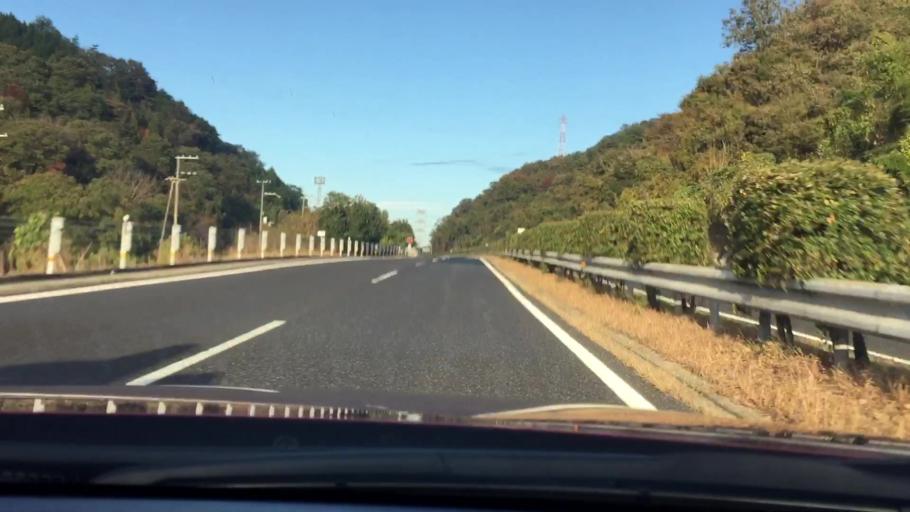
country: JP
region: Hyogo
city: Yamazakicho-nakabirose
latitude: 34.9795
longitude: 134.6244
